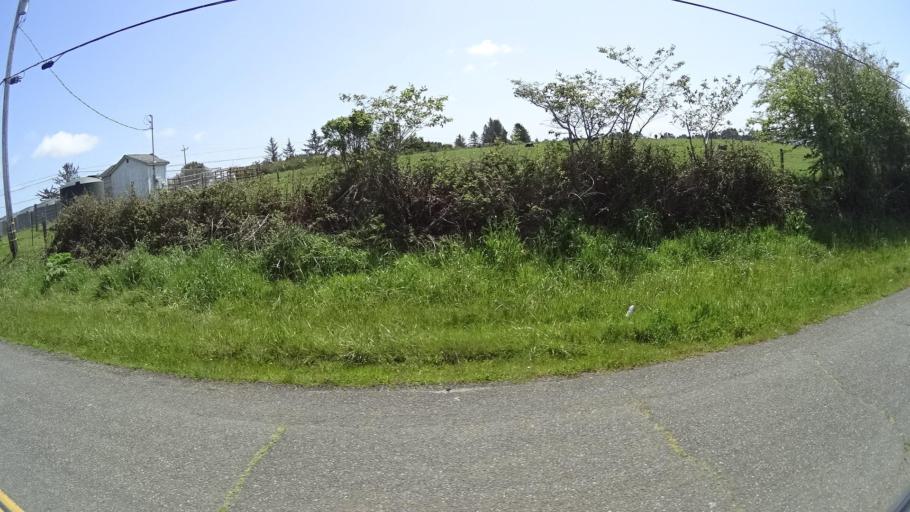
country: US
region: California
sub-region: Humboldt County
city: Fortuna
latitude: 40.6426
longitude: -124.2049
